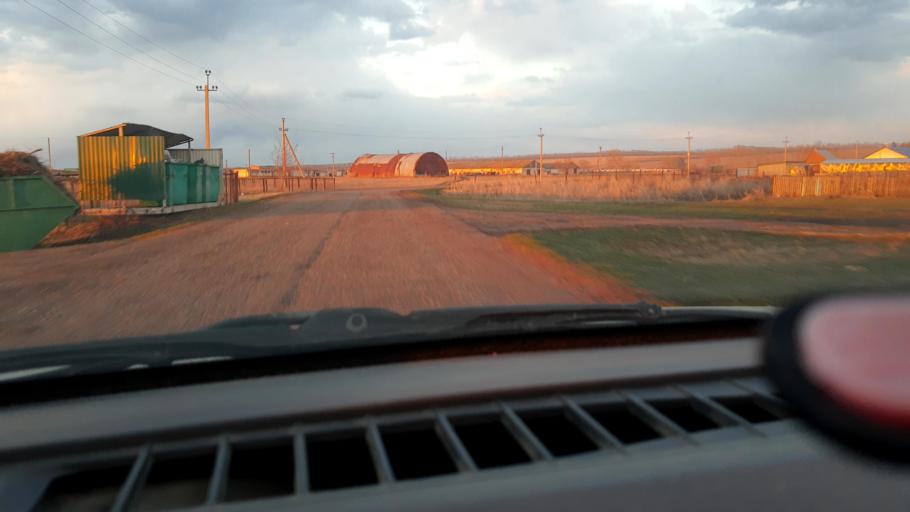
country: RU
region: Bashkortostan
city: Asanovo
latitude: 54.9092
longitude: 55.4900
